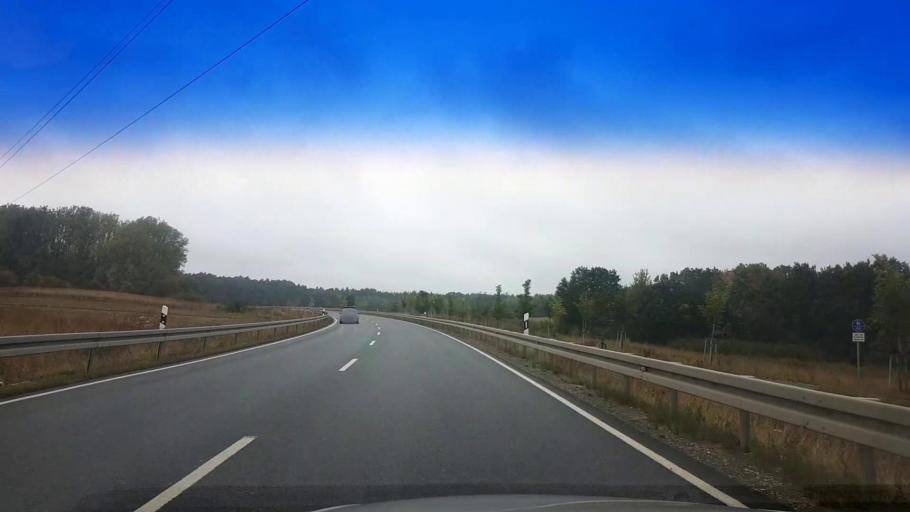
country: DE
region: Bavaria
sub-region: Upper Franconia
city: Hausen
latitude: 49.7024
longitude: 11.0385
